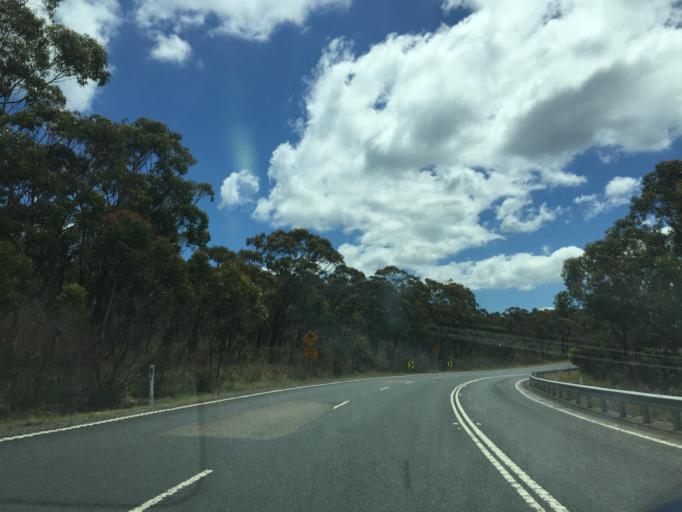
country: AU
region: New South Wales
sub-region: Blue Mountains Municipality
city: Blackheath
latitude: -33.5323
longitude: 150.3105
